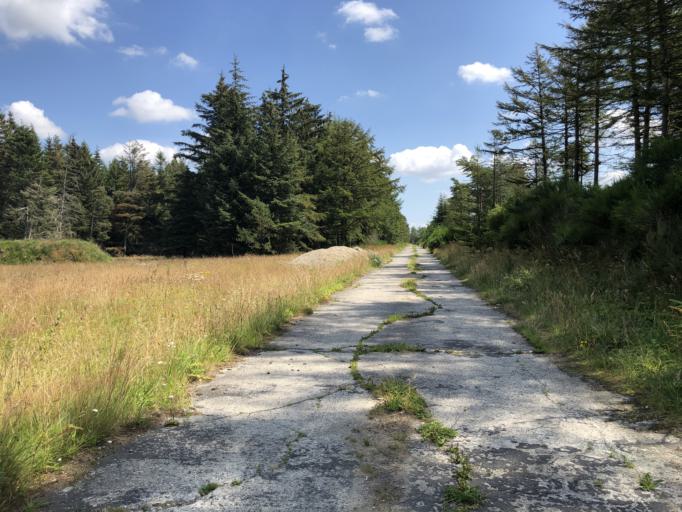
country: DK
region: Central Jutland
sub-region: Lemvig Kommune
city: Lemvig
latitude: 56.4965
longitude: 8.3249
